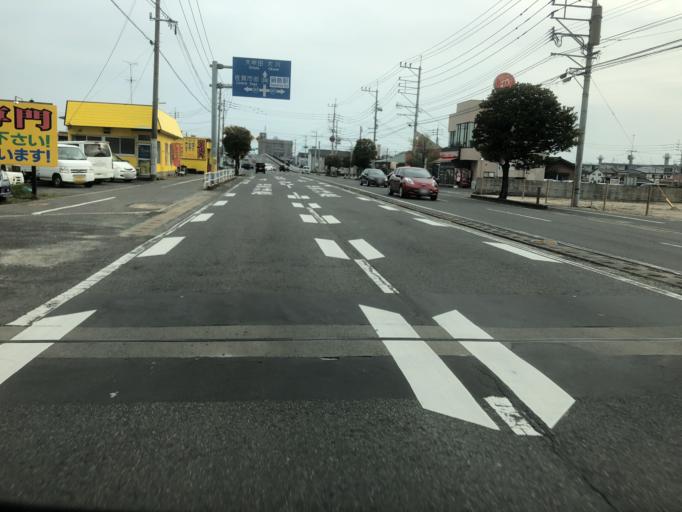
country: JP
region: Saga Prefecture
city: Saga-shi
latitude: 33.2630
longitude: 130.2724
